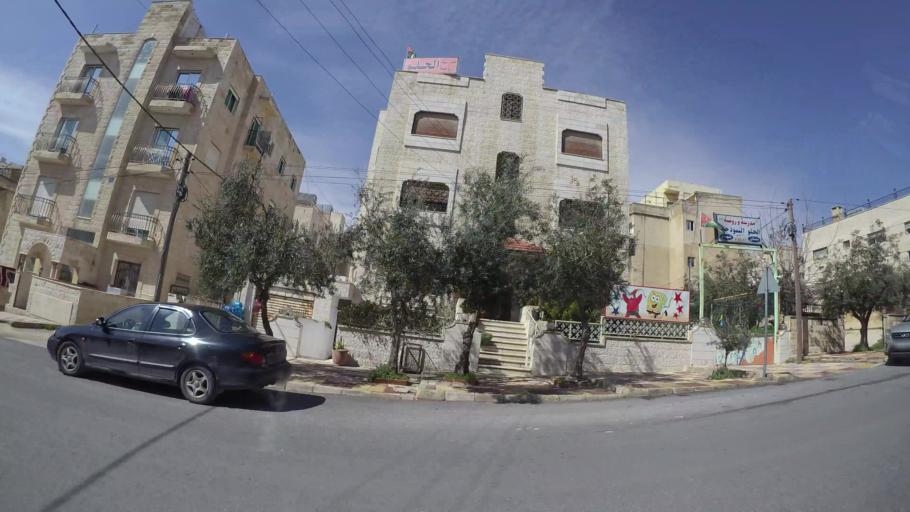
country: JO
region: Amman
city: Al Jubayhah
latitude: 31.9958
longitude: 35.9029
